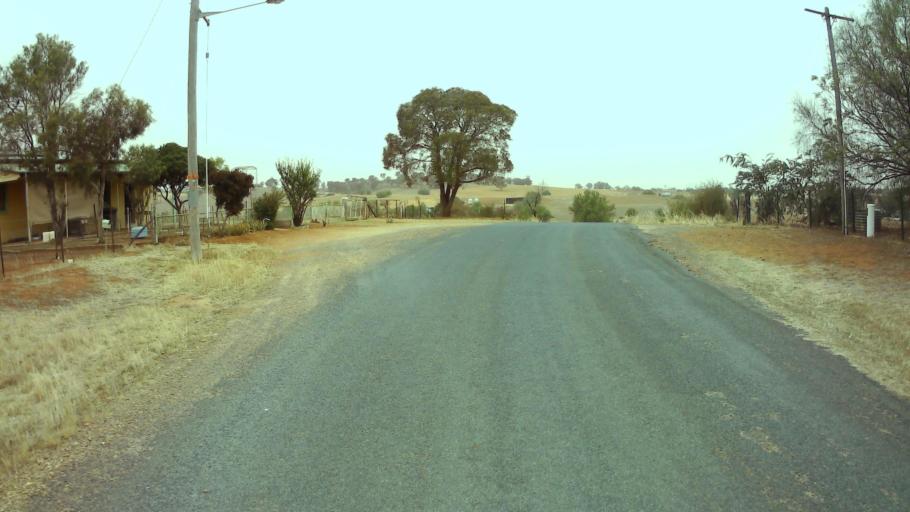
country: AU
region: New South Wales
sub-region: Weddin
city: Grenfell
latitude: -33.9022
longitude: 148.1696
